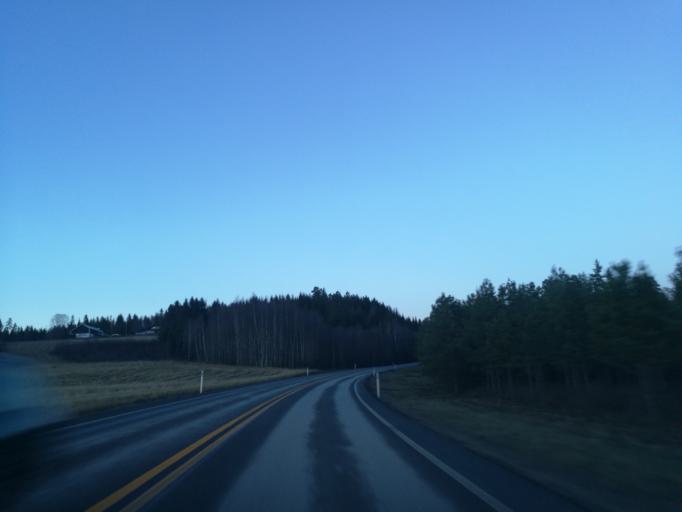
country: NO
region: Hedmark
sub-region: Eidskog
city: Skotterud
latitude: 59.9897
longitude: 12.1056
